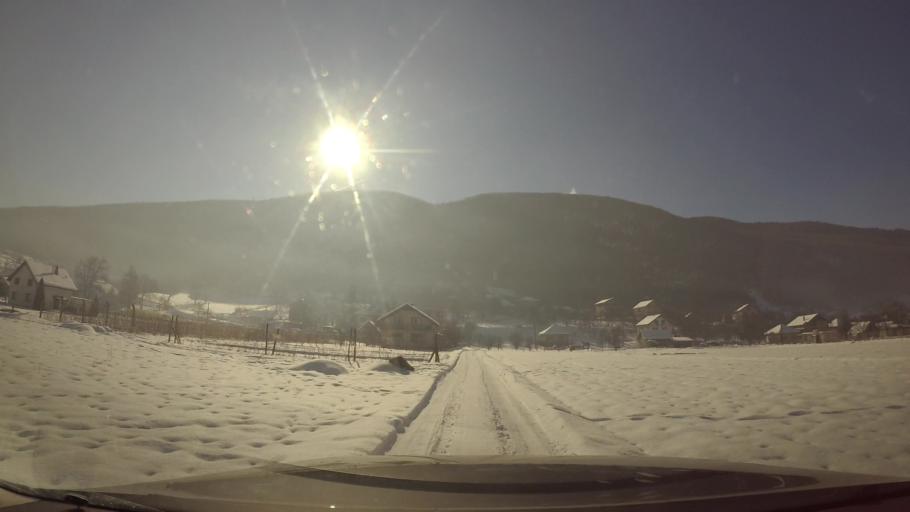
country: BA
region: Federation of Bosnia and Herzegovina
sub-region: Kanton Sarajevo
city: Sarajevo
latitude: 43.7894
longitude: 18.3409
